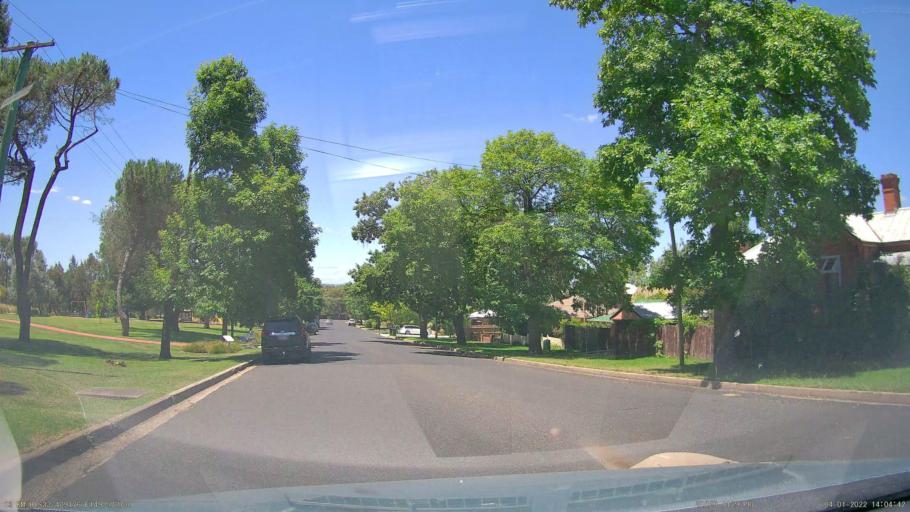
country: AU
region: New South Wales
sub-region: Bathurst Regional
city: Bathurst
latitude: -33.4092
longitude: 149.5739
